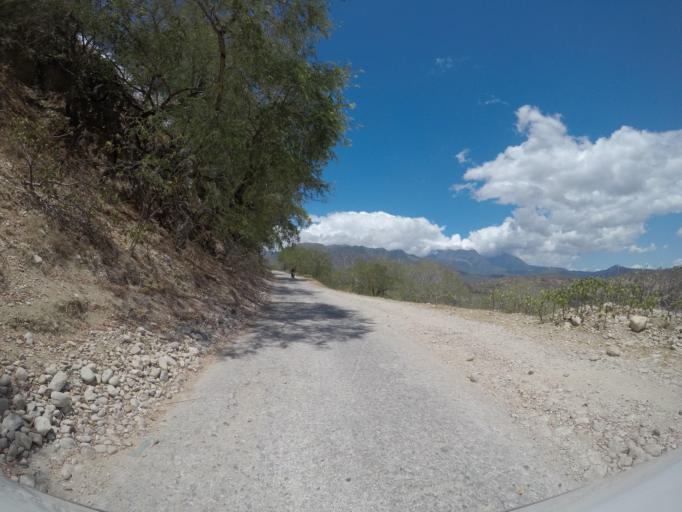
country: TL
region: Baucau
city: Baucau
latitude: -8.4798
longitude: 126.6051
